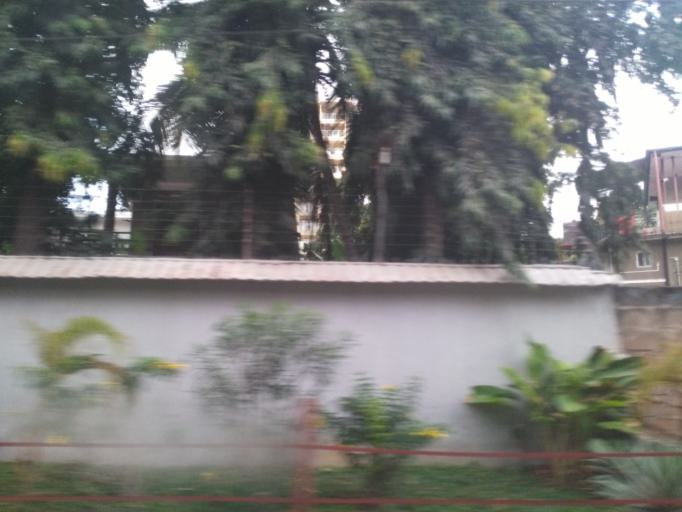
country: TZ
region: Dar es Salaam
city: Dar es Salaam
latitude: -6.8065
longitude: 39.2760
